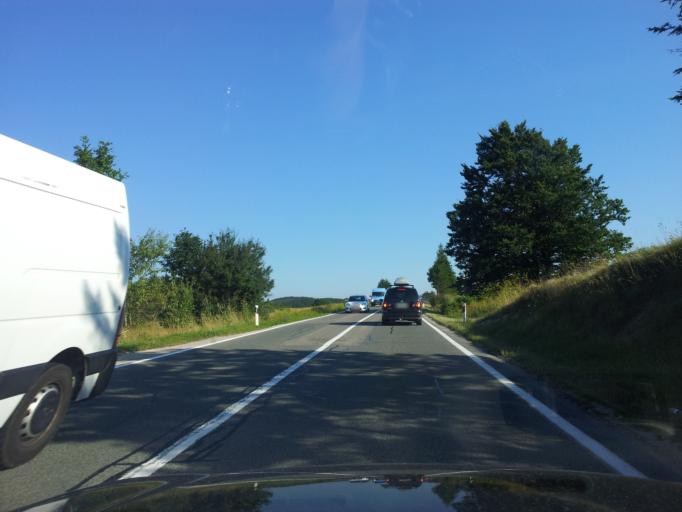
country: HR
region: Licko-Senjska
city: Jezerce
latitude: 44.8087
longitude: 15.6827
